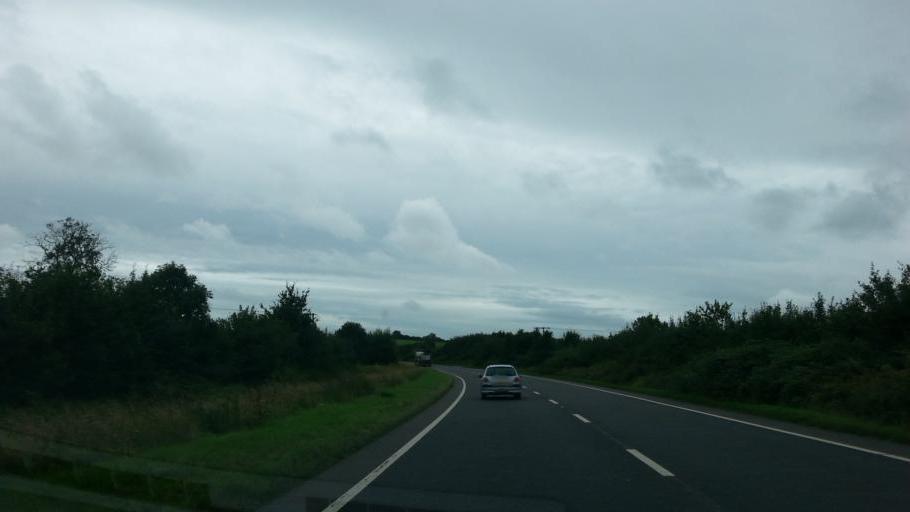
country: GB
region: England
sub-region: Wiltshire
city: Melksham
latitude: 51.3365
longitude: -2.1468
